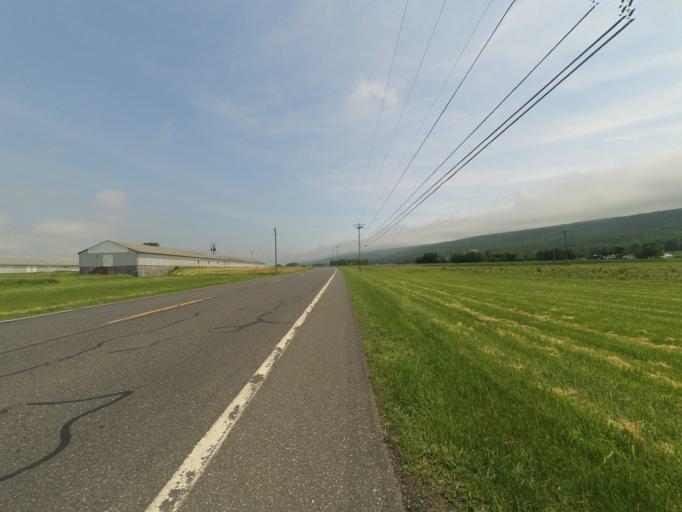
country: US
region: Pennsylvania
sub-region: Centre County
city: Pine Grove Mills
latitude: 40.7129
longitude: -77.9540
